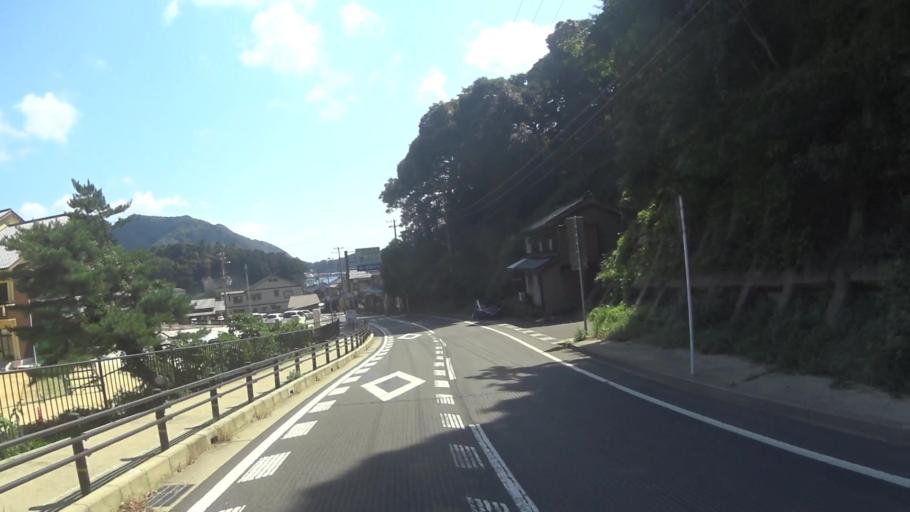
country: JP
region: Kyoto
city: Miyazu
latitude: 35.6784
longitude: 135.2864
